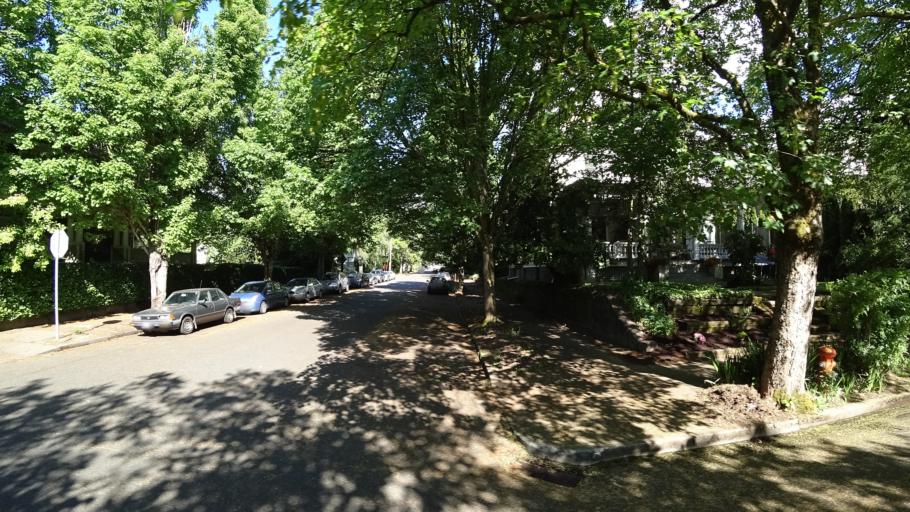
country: US
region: Oregon
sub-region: Multnomah County
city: Portland
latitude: 45.5186
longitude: -122.6496
